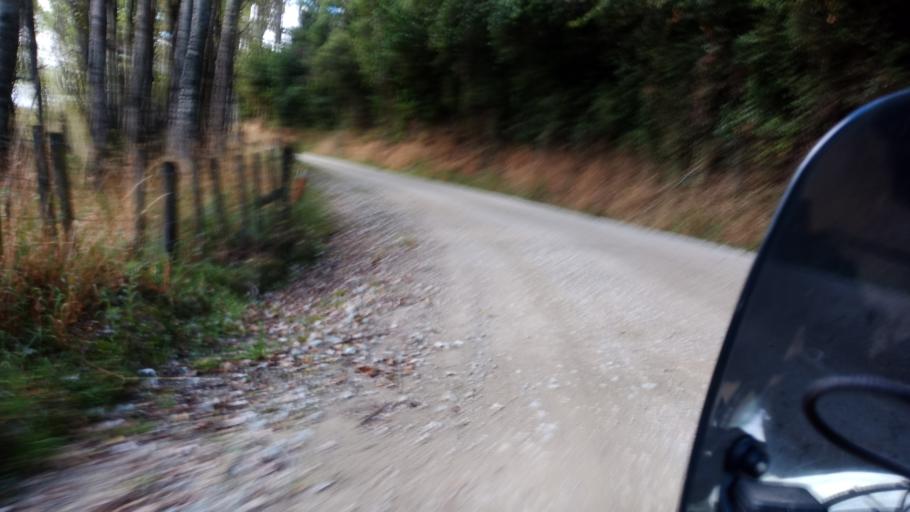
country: NZ
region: Hawke's Bay
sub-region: Wairoa District
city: Wairoa
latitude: -38.6062
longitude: 177.4642
